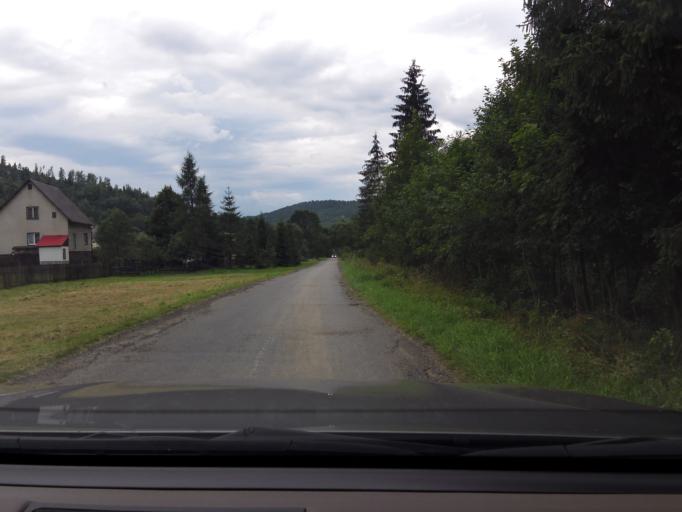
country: PL
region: Silesian Voivodeship
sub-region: Powiat zywiecki
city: Rajcza
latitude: 49.5021
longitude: 19.1217
